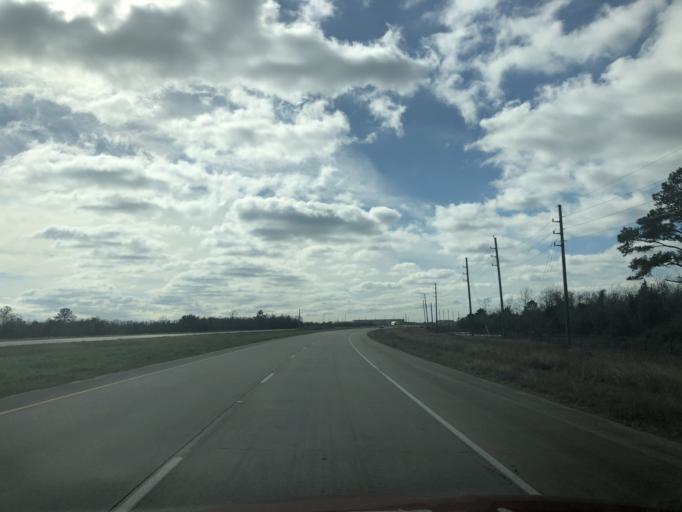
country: US
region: Texas
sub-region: Chambers County
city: Beach City
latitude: 29.7390
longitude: -94.8733
